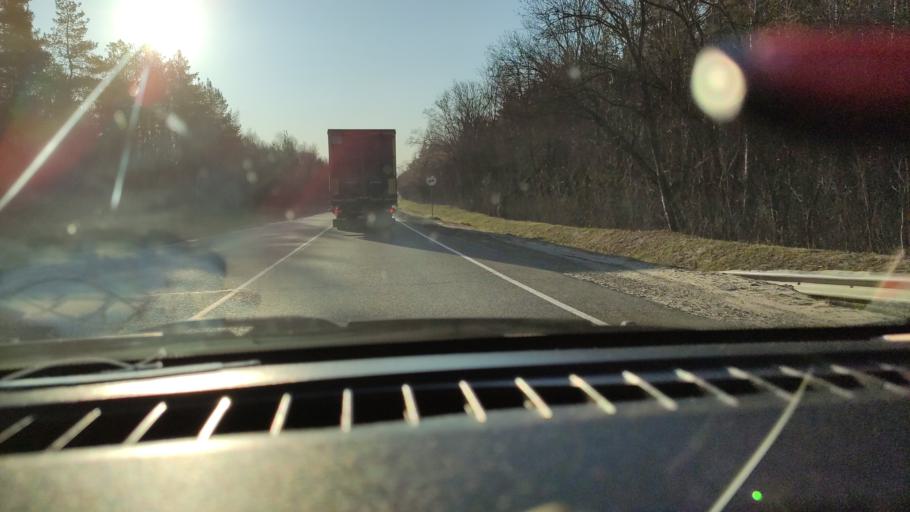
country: RU
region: Saratov
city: Vol'sk
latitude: 52.1059
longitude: 47.4330
